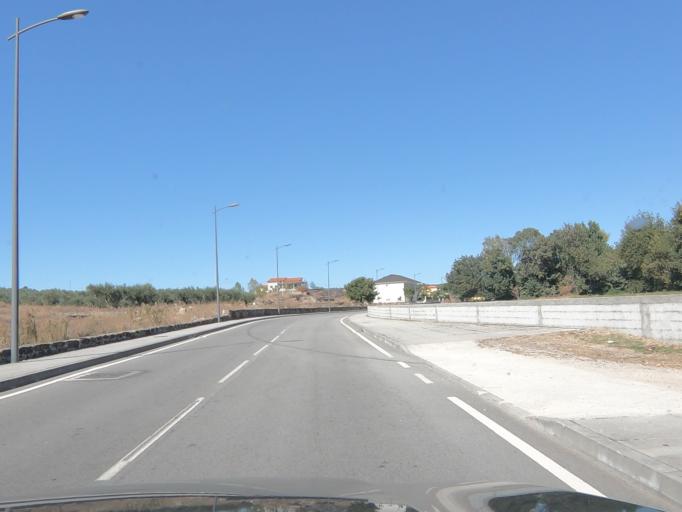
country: PT
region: Vila Real
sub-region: Valpacos
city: Valpacos
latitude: 41.5897
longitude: -7.3075
